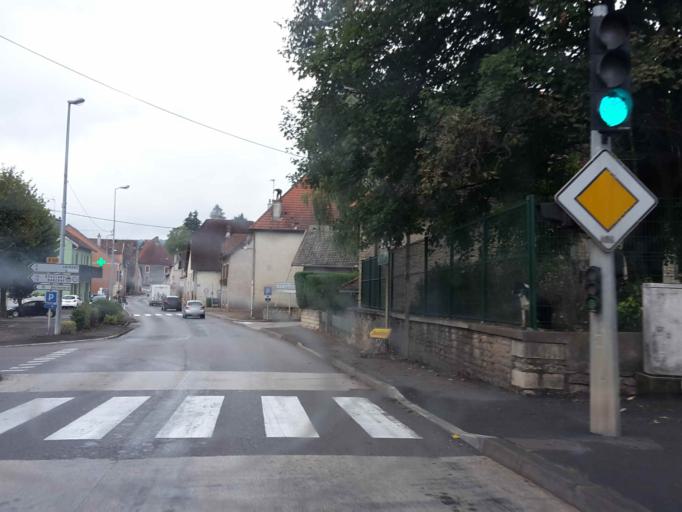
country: FR
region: Franche-Comte
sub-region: Departement du Doubs
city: Roulans
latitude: 47.3166
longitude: 6.2332
